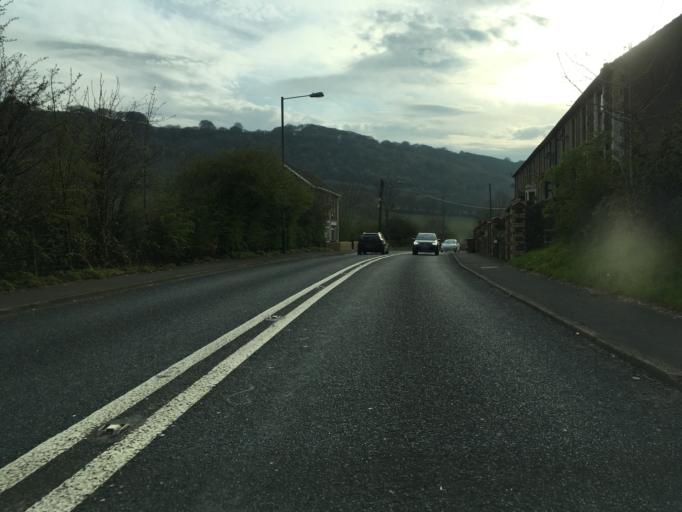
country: GB
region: Wales
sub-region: Caerphilly County Borough
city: Machen
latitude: 51.6135
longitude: -3.1557
